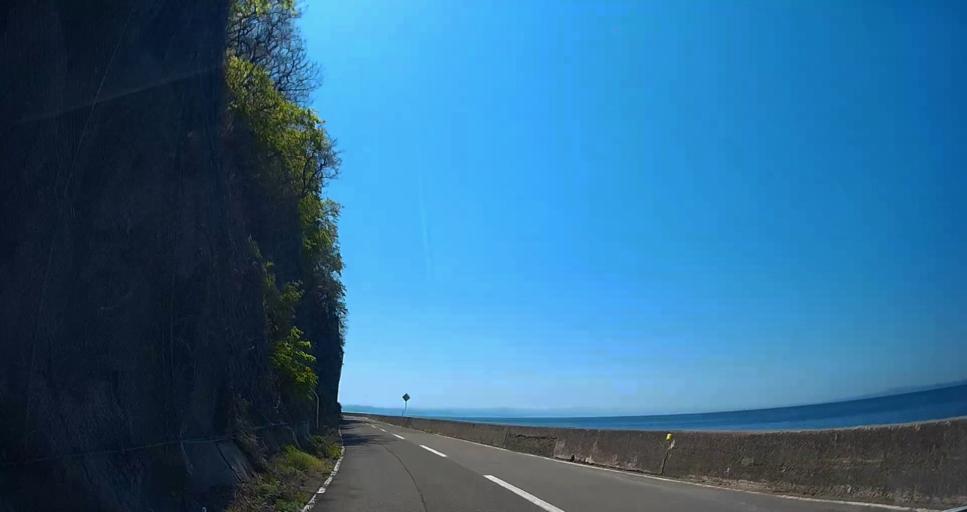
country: JP
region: Aomori
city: Aomori Shi
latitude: 41.1358
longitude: 140.7775
